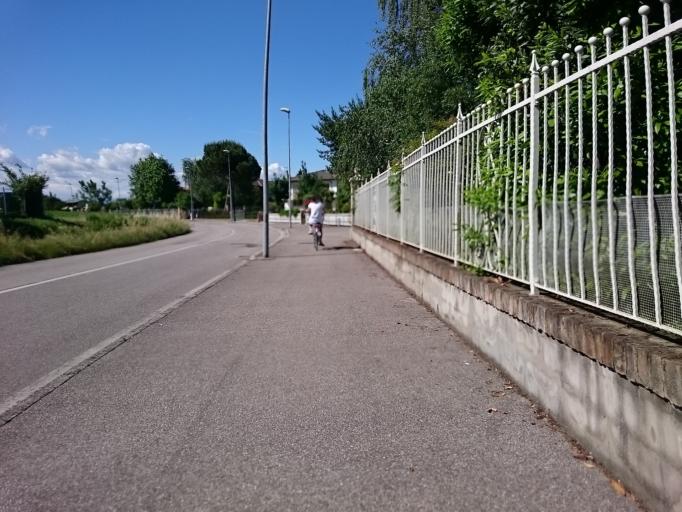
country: IT
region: Veneto
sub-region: Provincia di Venezia
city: Campolongo Maggiore Liettoli
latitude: 45.3437
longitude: 12.0193
